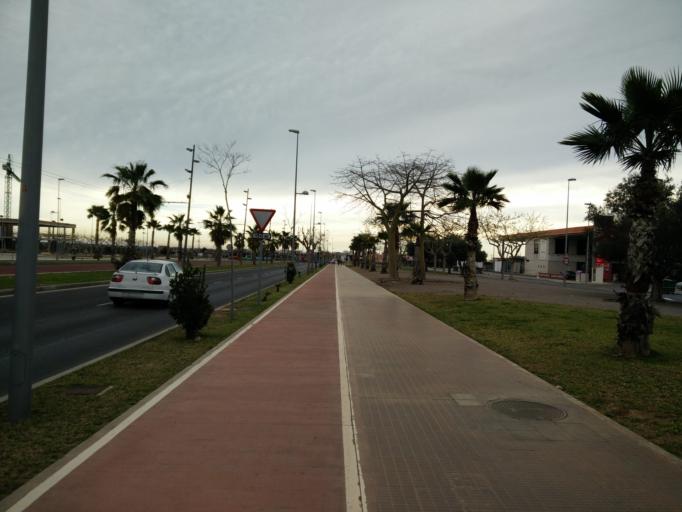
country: ES
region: Valencia
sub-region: Provincia de Castello
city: Castello de la Plana
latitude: 39.9826
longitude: -0.0197
